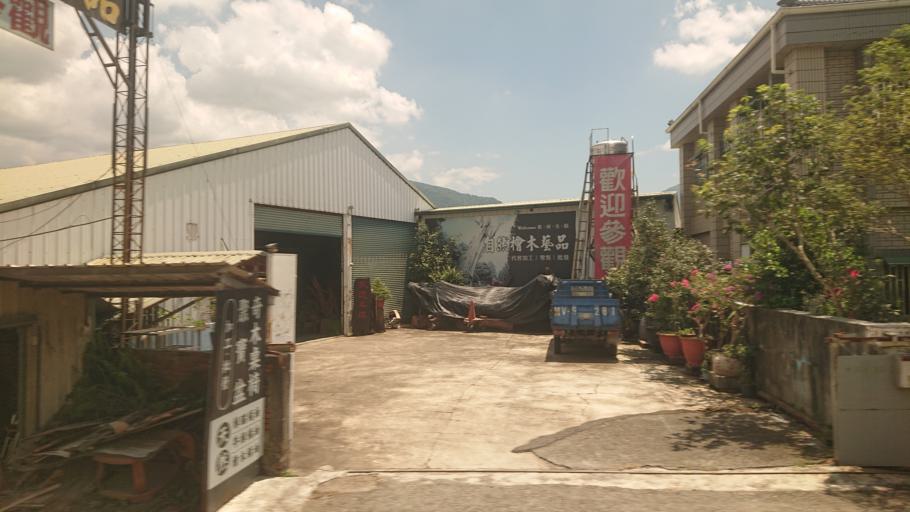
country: TW
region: Taiwan
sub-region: Nantou
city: Puli
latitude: 23.9817
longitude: 120.9602
